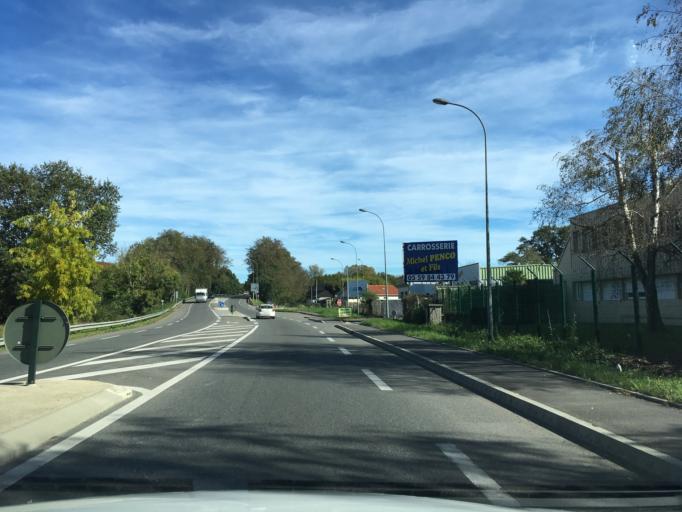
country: FR
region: Aquitaine
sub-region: Departement des Pyrenees-Atlantiques
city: Buros
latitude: 43.3208
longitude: -0.3038
